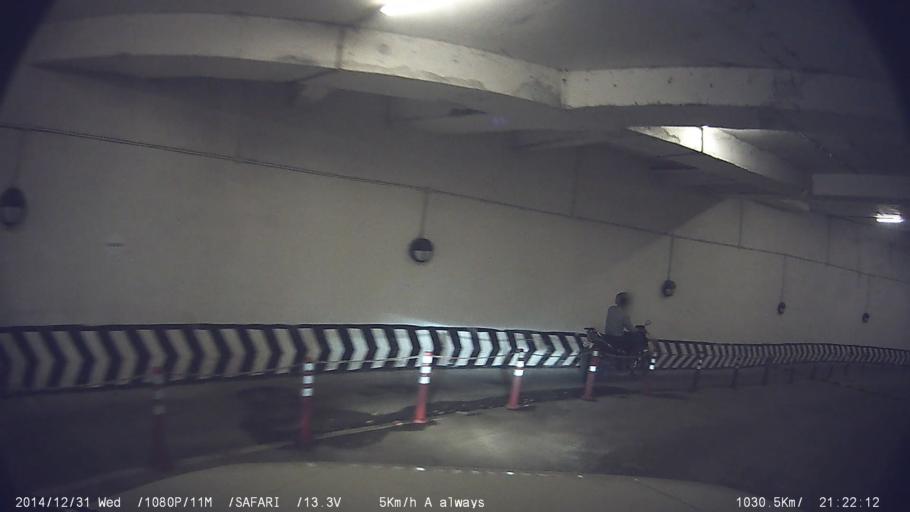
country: IN
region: Tamil Nadu
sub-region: Kancheepuram
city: Alandur
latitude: 12.9920
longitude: 80.2174
